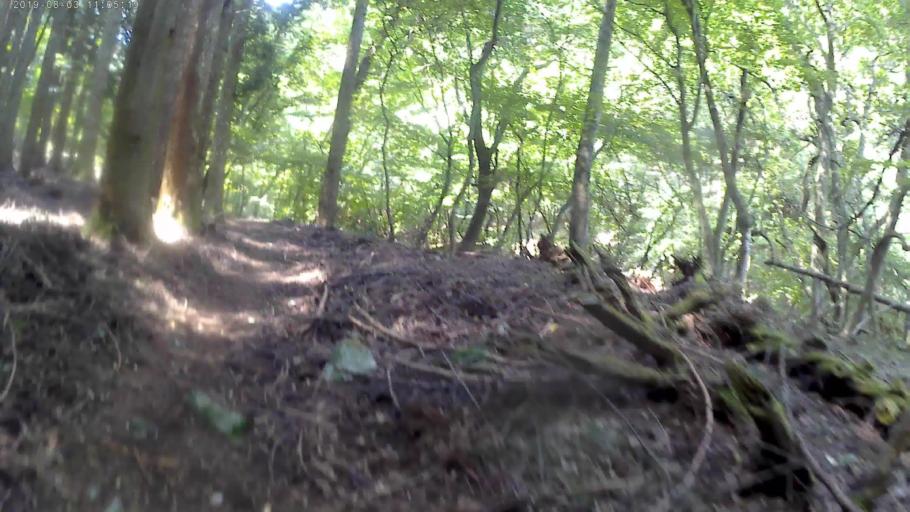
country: JP
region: Yamanashi
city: Enzan
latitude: 35.6179
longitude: 138.7741
